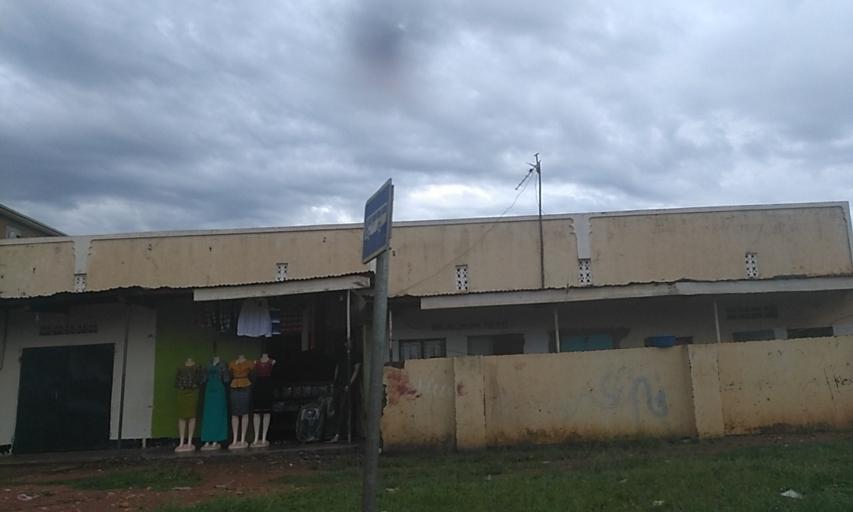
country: UG
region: Central Region
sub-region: Wakiso District
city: Bweyogerere
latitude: 0.3942
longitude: 32.6637
